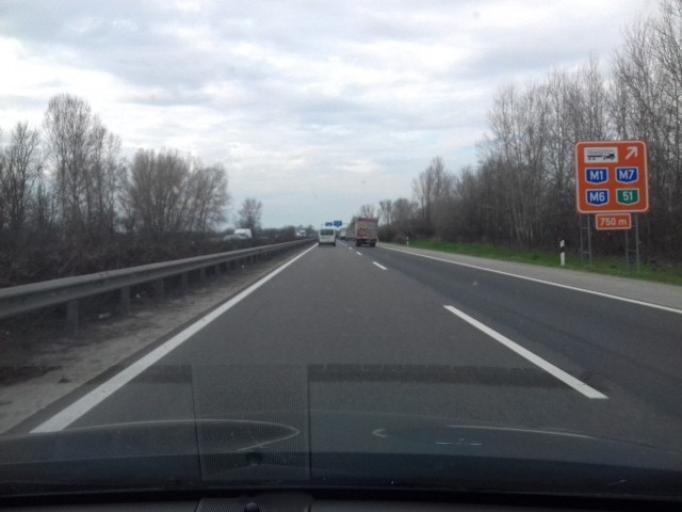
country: HU
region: Pest
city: Gyal
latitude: 47.3839
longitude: 19.1774
